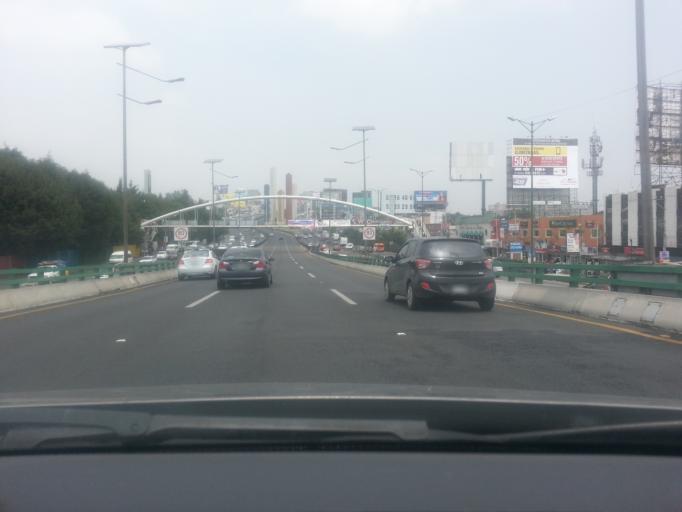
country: MX
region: Mexico
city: Naucalpan de Juarez
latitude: 19.4946
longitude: -99.2369
